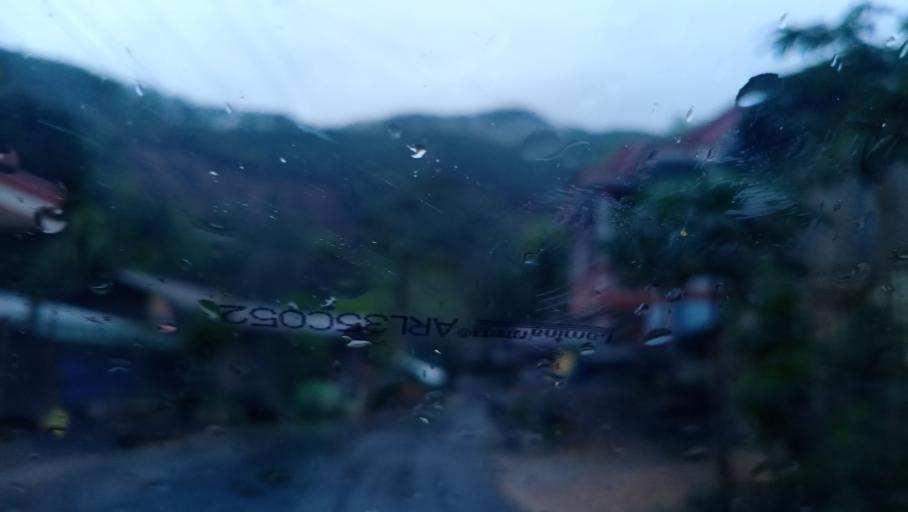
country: LA
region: Phongsali
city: Khoa
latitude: 21.0753
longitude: 102.5023
